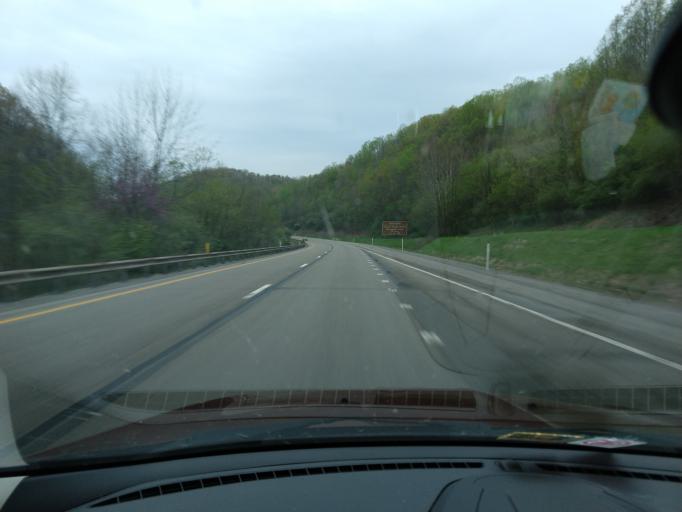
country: US
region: West Virginia
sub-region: Lewis County
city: Weston
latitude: 39.0124
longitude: -80.4636
